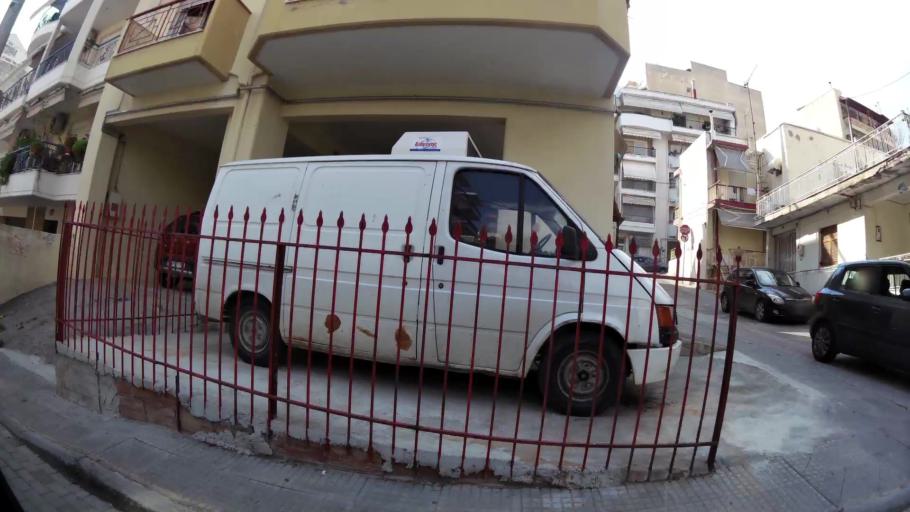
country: GR
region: Central Macedonia
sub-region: Nomos Thessalonikis
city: Sykies
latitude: 40.6586
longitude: 22.9578
